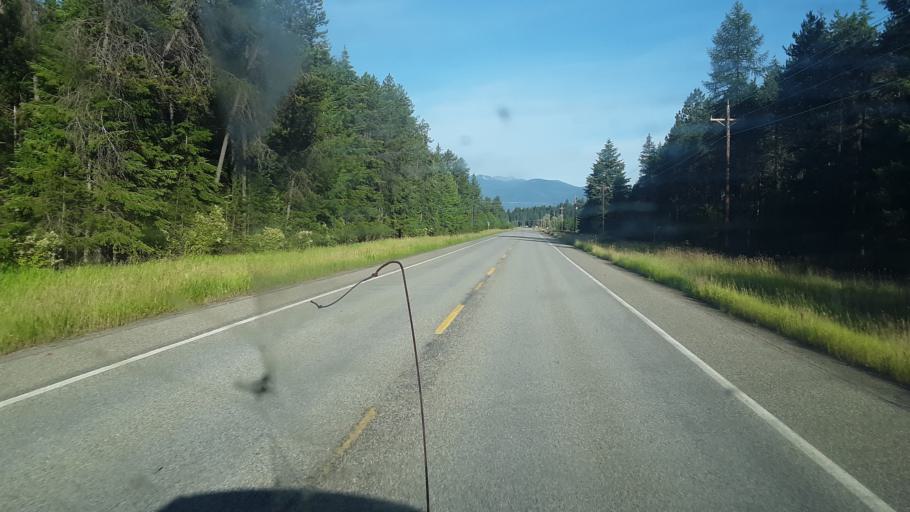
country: US
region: Idaho
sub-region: Boundary County
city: Bonners Ferry
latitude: 48.7292
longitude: -116.2293
